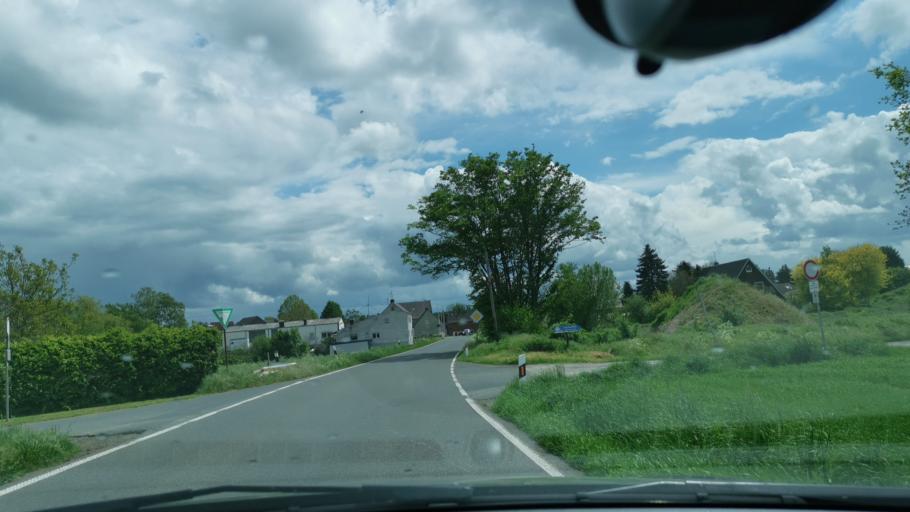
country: DE
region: North Rhine-Westphalia
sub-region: Regierungsbezirk Dusseldorf
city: Rommerskirchen
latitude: 51.0865
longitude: 6.6862
